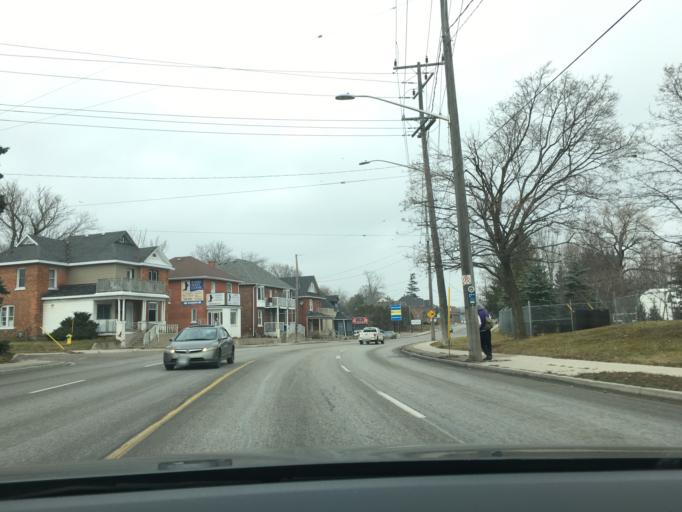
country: CA
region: Ontario
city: Barrie
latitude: 44.3771
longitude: -79.6933
